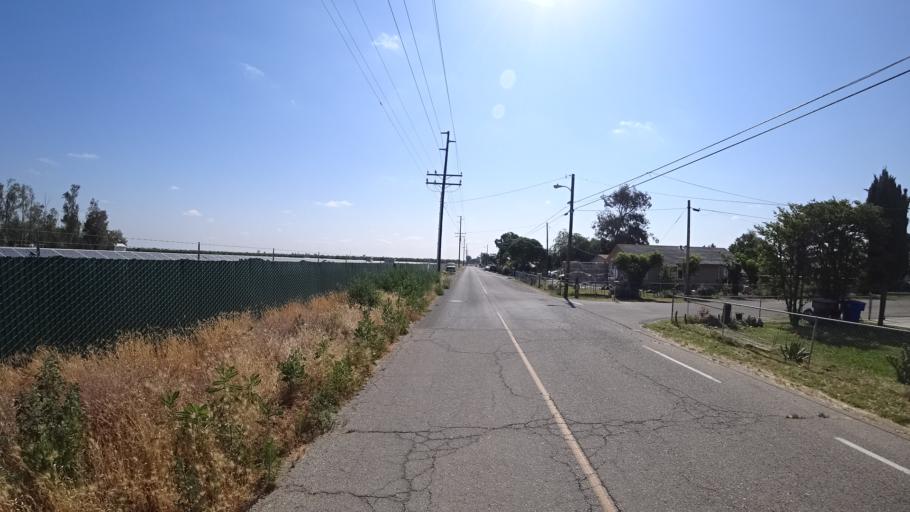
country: US
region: California
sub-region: Kings County
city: Home Garden
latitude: 36.3059
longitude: -119.6313
